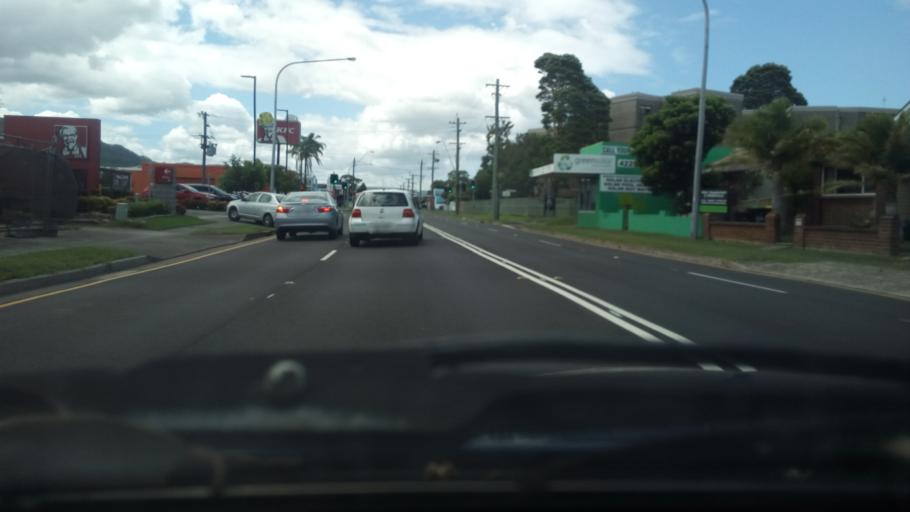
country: AU
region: New South Wales
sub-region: Wollongong
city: Fairy Meadow
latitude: -34.4014
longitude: 150.8916
